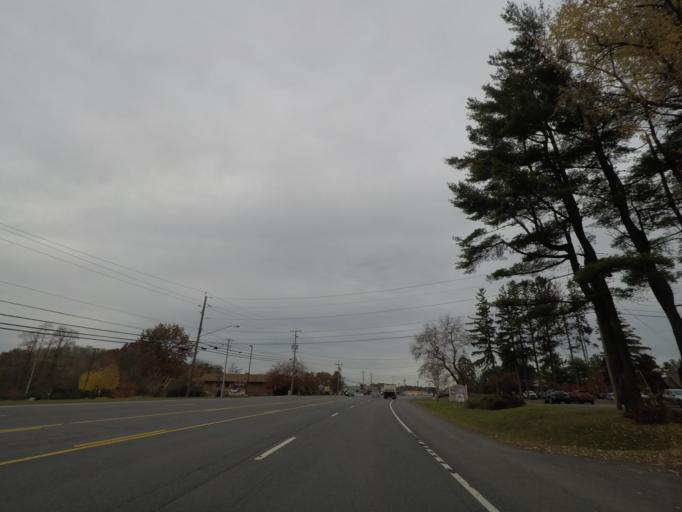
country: US
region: New York
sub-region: Saratoga County
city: Country Knolls
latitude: 42.8690
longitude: -73.7732
